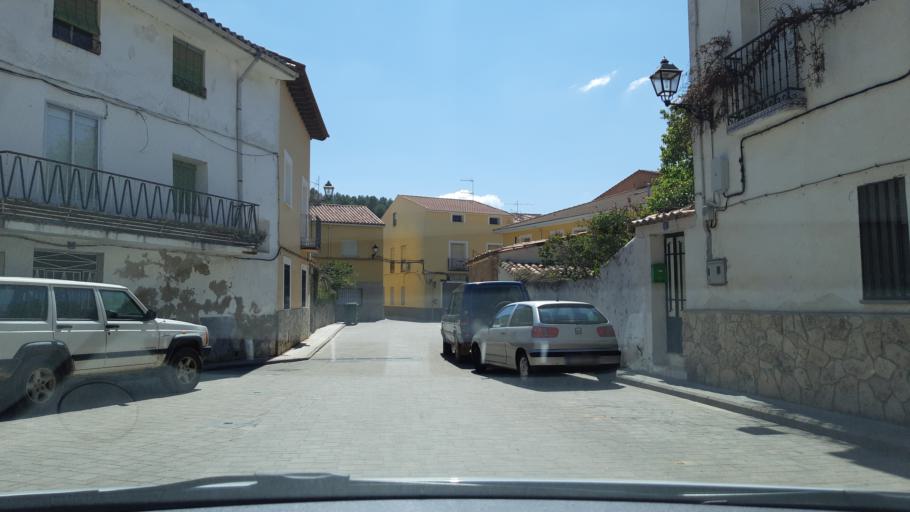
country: ES
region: Castille-La Mancha
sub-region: Provincia de Guadalajara
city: Cifuentes
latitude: 40.7863
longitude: -2.6211
